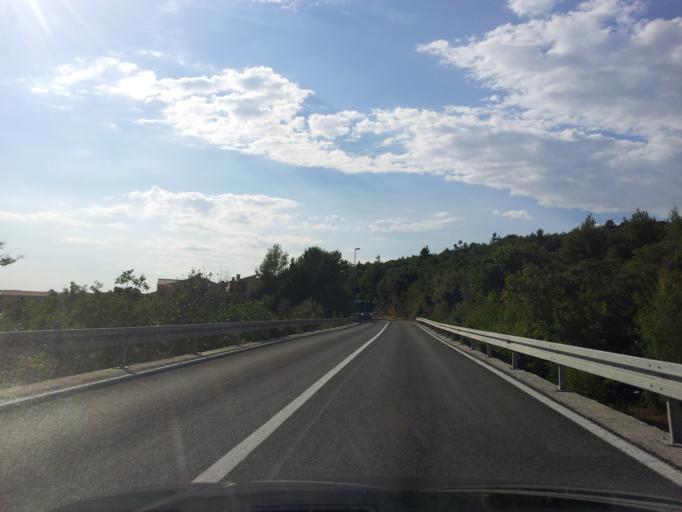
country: HR
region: Zadarska
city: Posedarje
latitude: 44.2126
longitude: 15.4920
